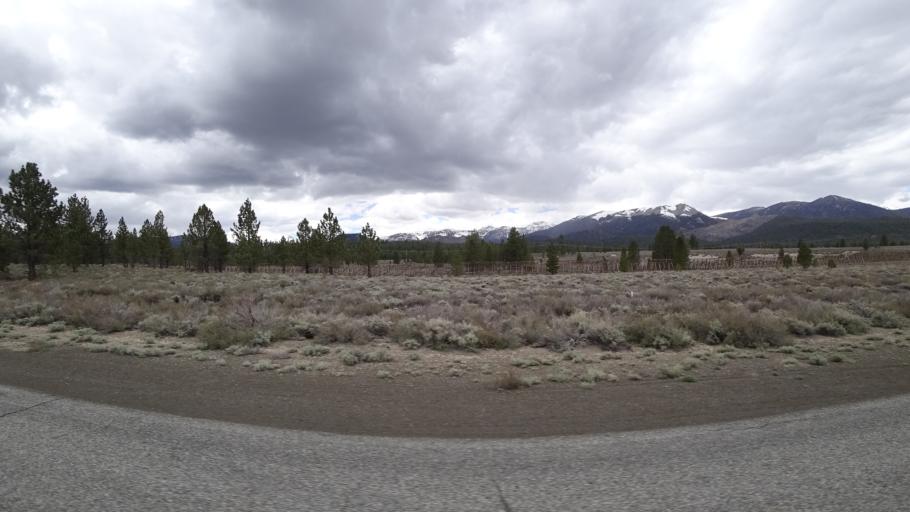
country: US
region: California
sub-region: Mono County
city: Mammoth Lakes
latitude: 37.7365
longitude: -118.9718
